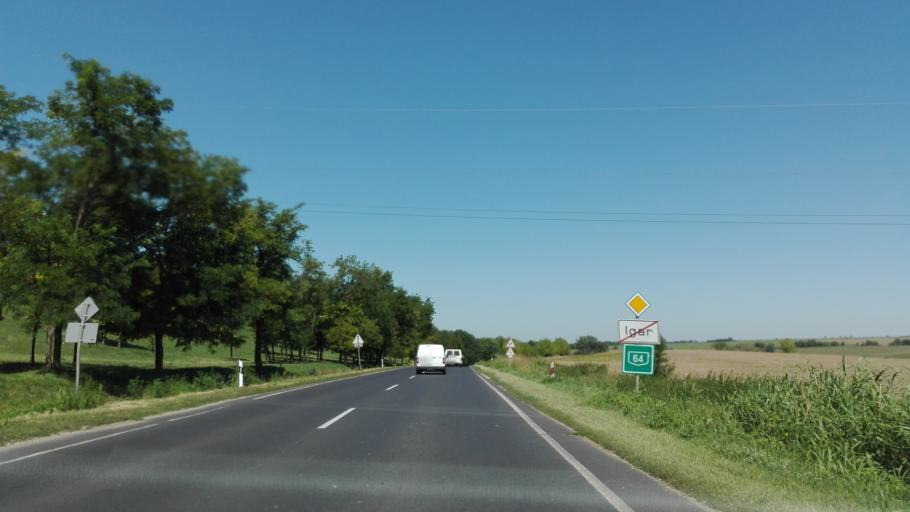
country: HU
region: Fejer
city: Mezoszilas
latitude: 46.7844
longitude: 18.5068
